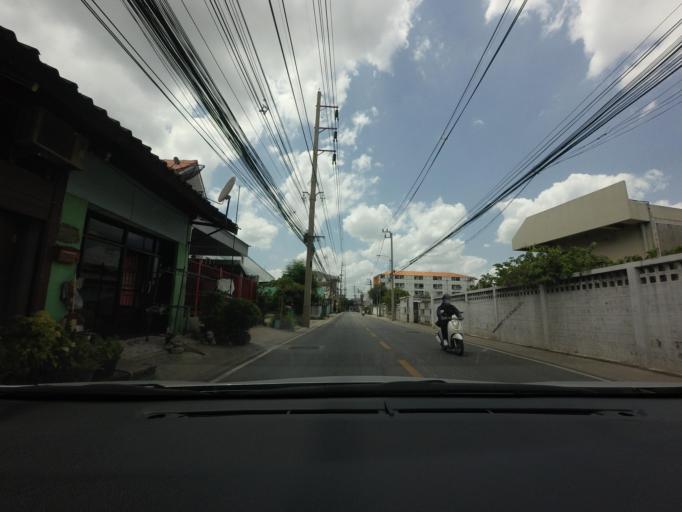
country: TH
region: Samut Prakan
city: Phra Samut Chedi
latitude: 13.6439
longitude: 100.5787
